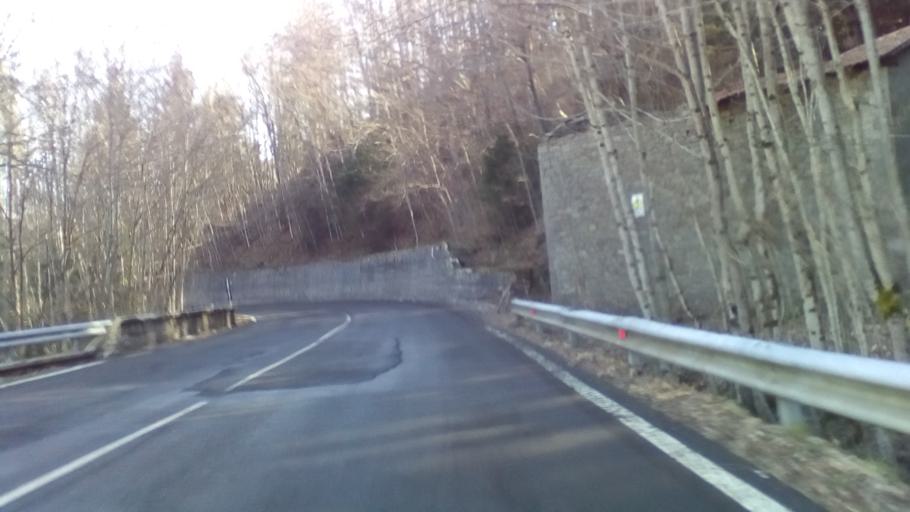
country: IT
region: Emilia-Romagna
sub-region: Provincia di Modena
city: Pievepelago
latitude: 44.1883
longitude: 10.5749
